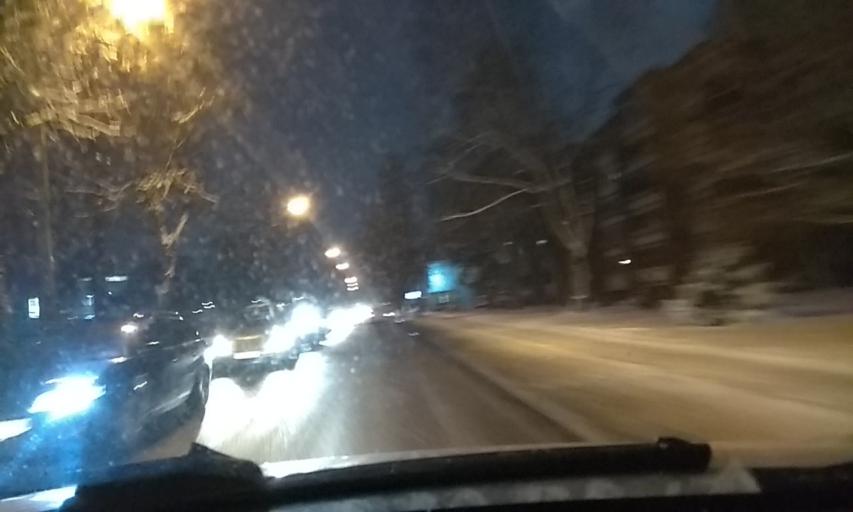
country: LT
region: Kauno apskritis
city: Dainava (Kaunas)
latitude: 54.9064
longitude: 23.9511
